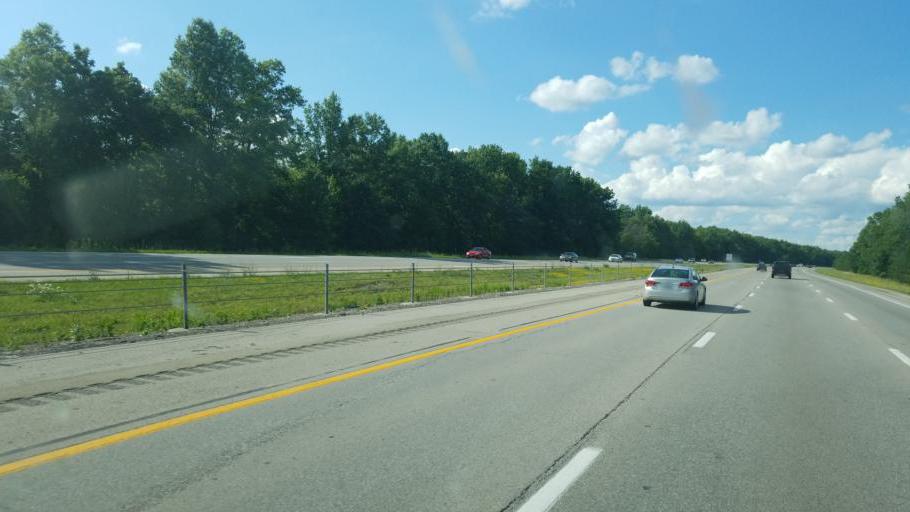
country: US
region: Ohio
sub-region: Delaware County
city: Sunbury
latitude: 40.2921
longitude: -82.9248
